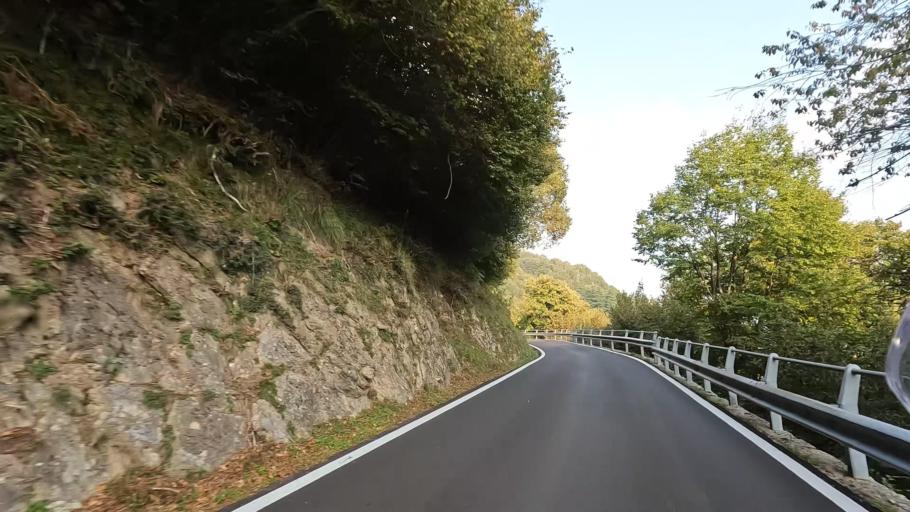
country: IT
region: Lombardy
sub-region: Provincia di Como
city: Dizzasco-Biazzeno
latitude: 45.9523
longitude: 9.1080
